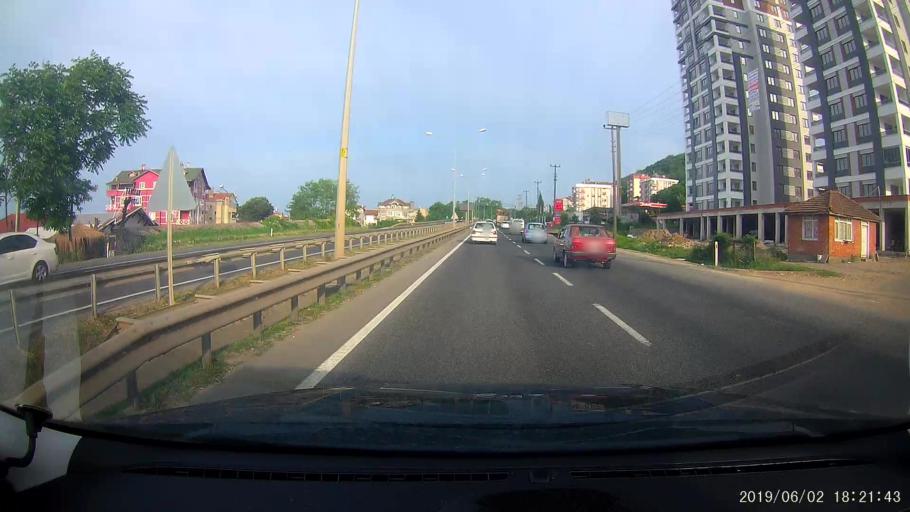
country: TR
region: Ordu
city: Fatsa
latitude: 41.0626
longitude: 37.4714
